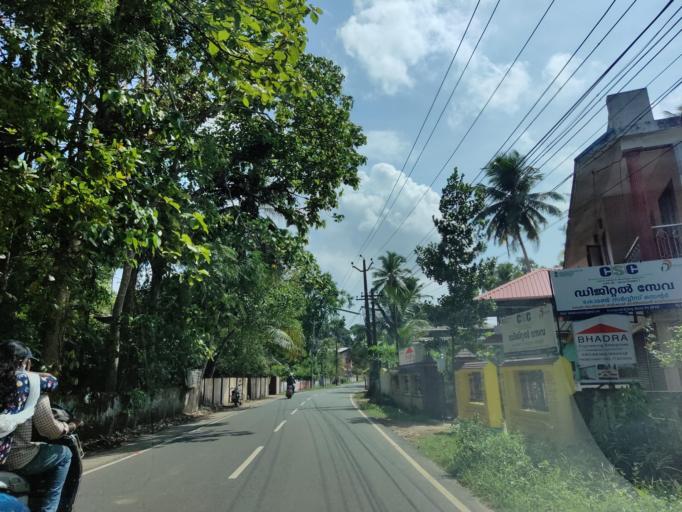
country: IN
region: Kerala
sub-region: Alappuzha
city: Mavelikara
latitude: 9.3193
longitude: 76.5300
